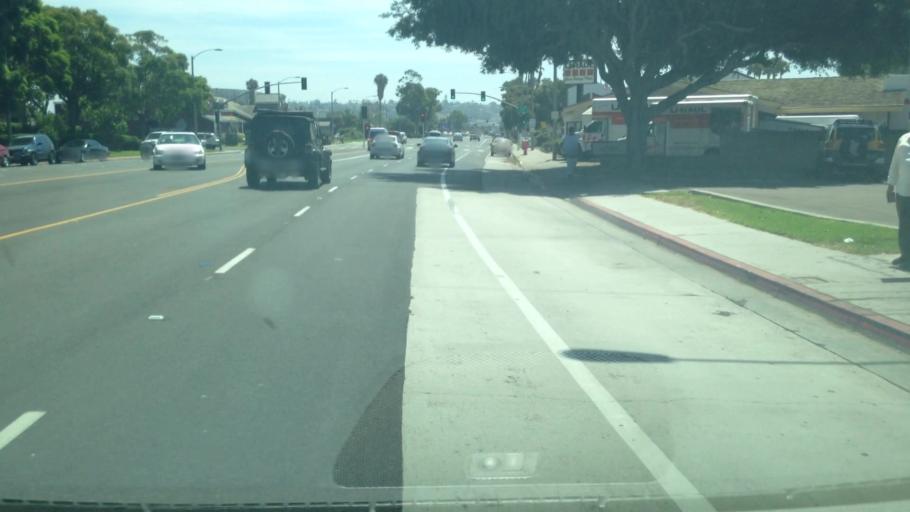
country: US
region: California
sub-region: San Diego County
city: San Diego
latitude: 32.7548
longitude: -117.2185
